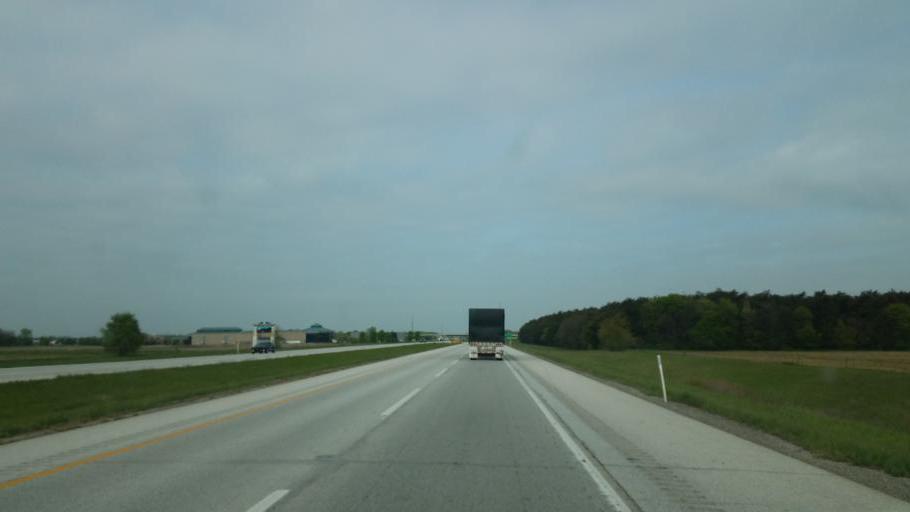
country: US
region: Indiana
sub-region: Elkhart County
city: Bristol
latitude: 41.7310
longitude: -85.8731
